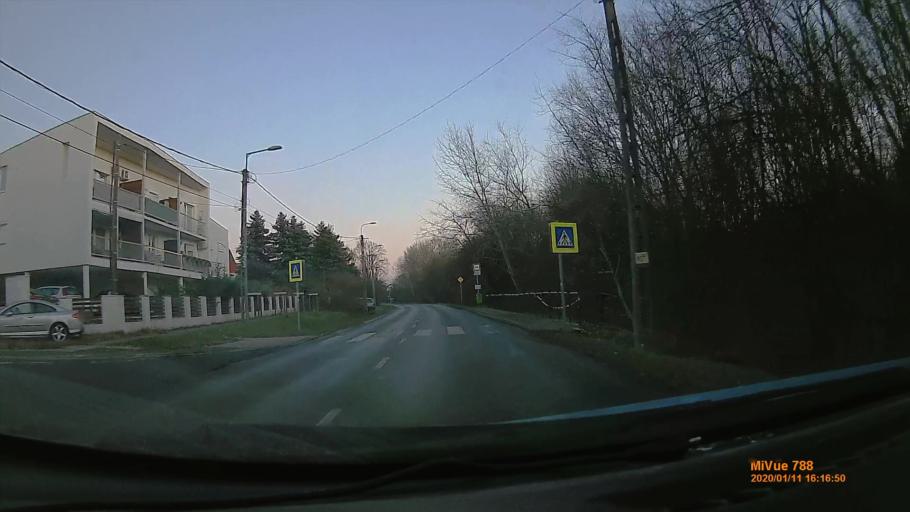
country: HU
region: Budapest
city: Budapest XVI. keruelet
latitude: 47.5248
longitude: 19.2048
